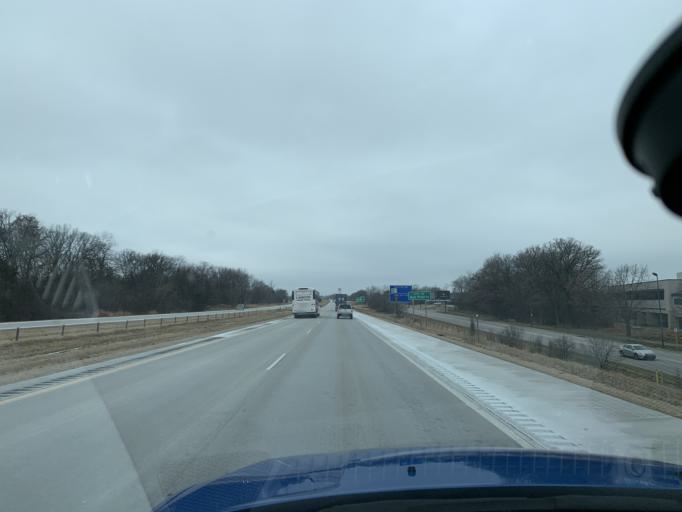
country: US
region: Wisconsin
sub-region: Dane County
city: Sun Prairie
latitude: 43.2002
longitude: -89.2008
